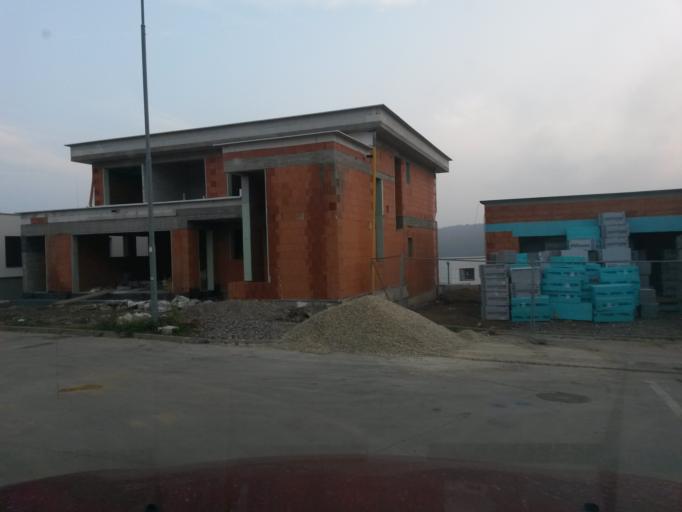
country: SK
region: Kosicky
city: Kosice
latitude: 48.7171
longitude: 21.2000
